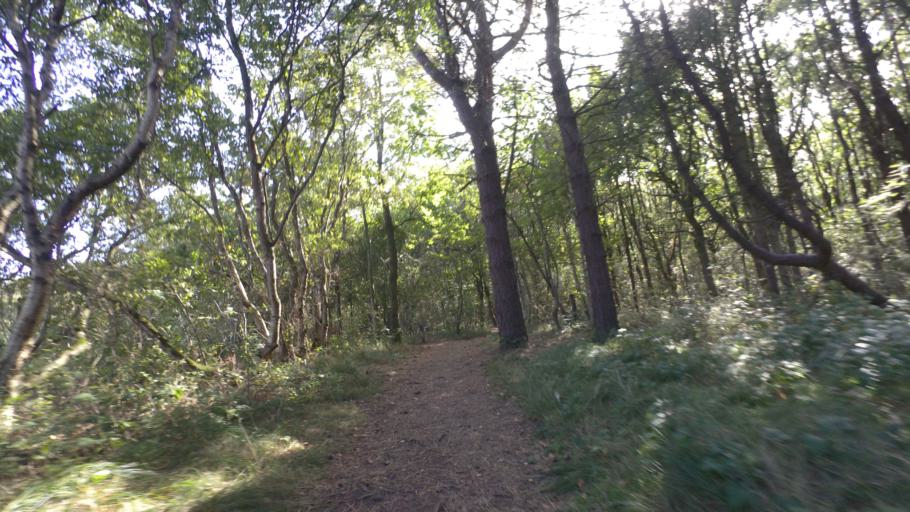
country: NL
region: Friesland
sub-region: Gemeente Ameland
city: Hollum
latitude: 53.4490
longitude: 5.7014
